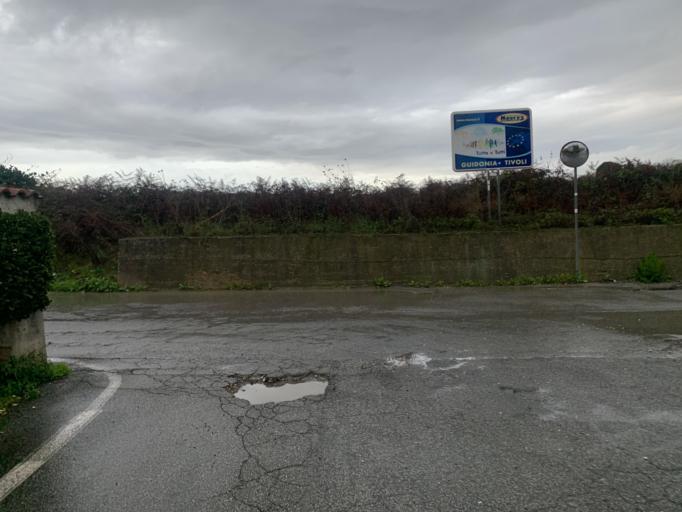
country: IT
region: Latium
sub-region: Citta metropolitana di Roma Capitale
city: Setteville
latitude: 41.9453
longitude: 12.6521
